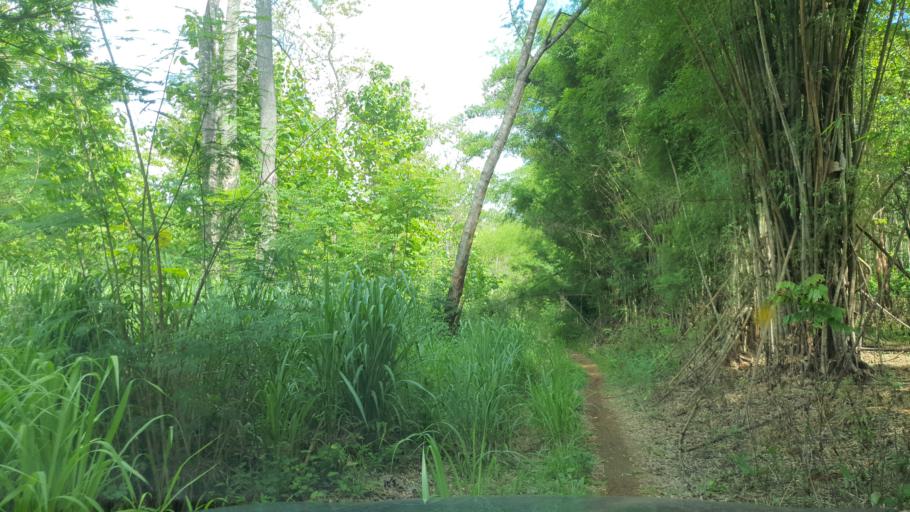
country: TH
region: Chiang Mai
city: Mae Taeng
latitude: 19.0739
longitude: 99.0995
